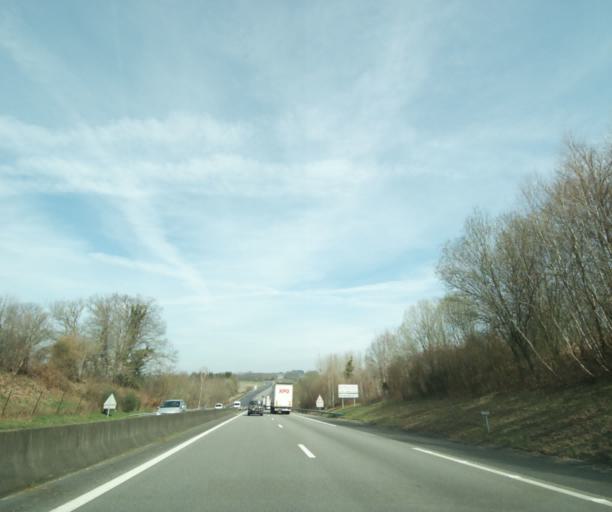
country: FR
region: Limousin
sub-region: Departement de la Correze
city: Uzerche
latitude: 45.3758
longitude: 1.5739
